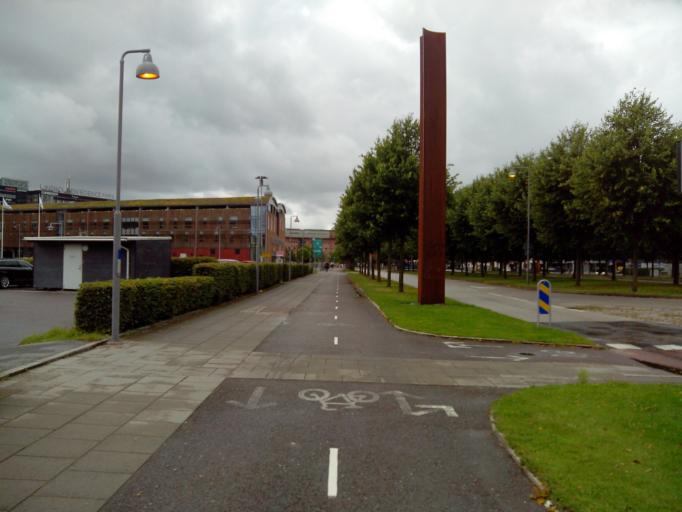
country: SE
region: Vaestra Goetaland
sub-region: Goteborg
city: Goeteborg
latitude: 57.7094
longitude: 11.9410
